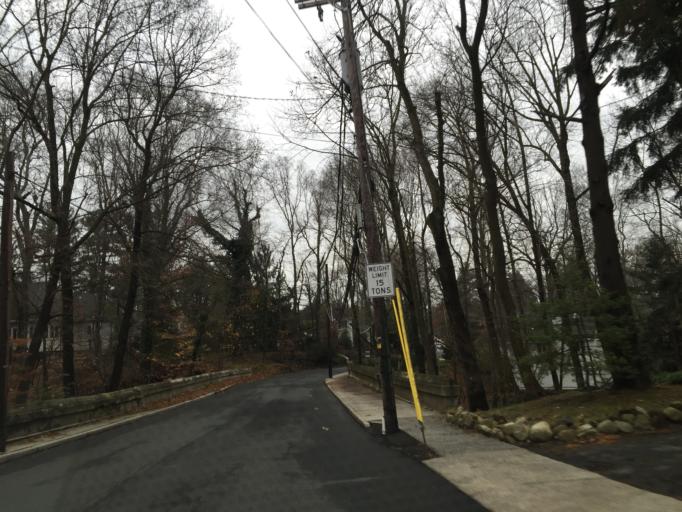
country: US
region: New Jersey
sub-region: Morris County
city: Chatham
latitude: 40.7135
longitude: -74.3727
